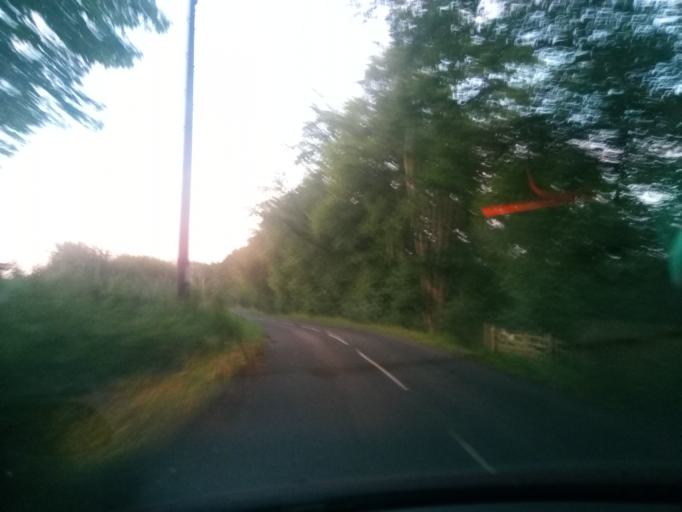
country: GB
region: England
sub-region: Northumberland
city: Wall
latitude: 54.9934
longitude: -2.2094
